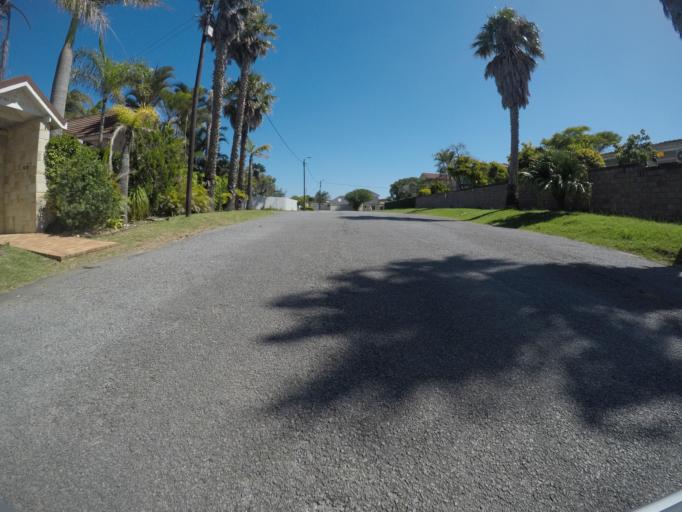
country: ZA
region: Eastern Cape
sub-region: Buffalo City Metropolitan Municipality
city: East London
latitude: -32.9842
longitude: 27.9314
